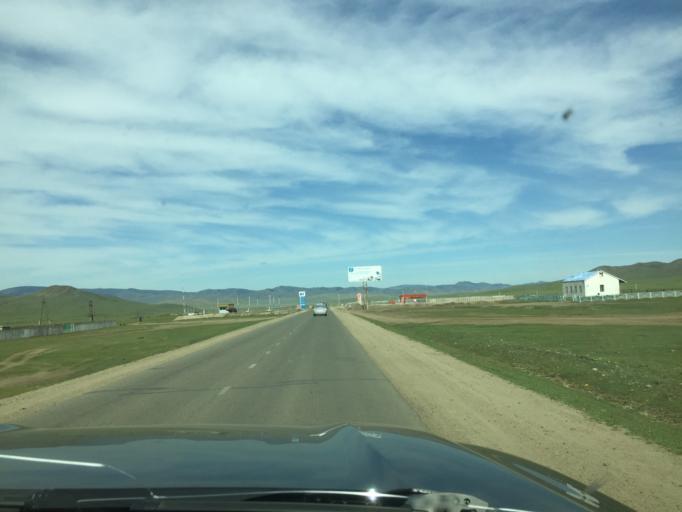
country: MN
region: Central Aimak
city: Ihsueuej
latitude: 48.2278
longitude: 106.2875
